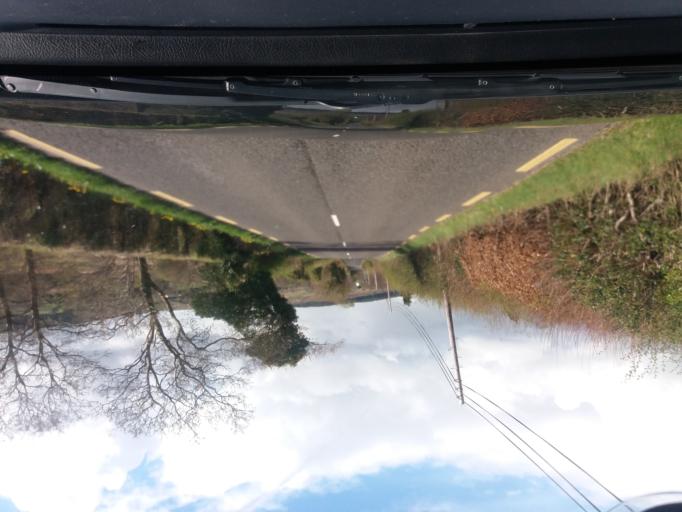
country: IE
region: Connaught
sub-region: County Leitrim
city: Manorhamilton
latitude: 54.3562
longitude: -8.2516
